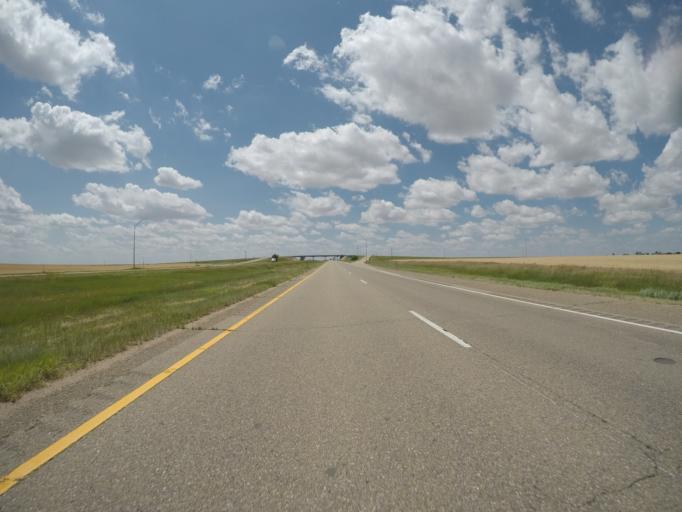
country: US
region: Colorado
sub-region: Kit Carson County
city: Burlington
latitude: 39.2942
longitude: -102.4230
